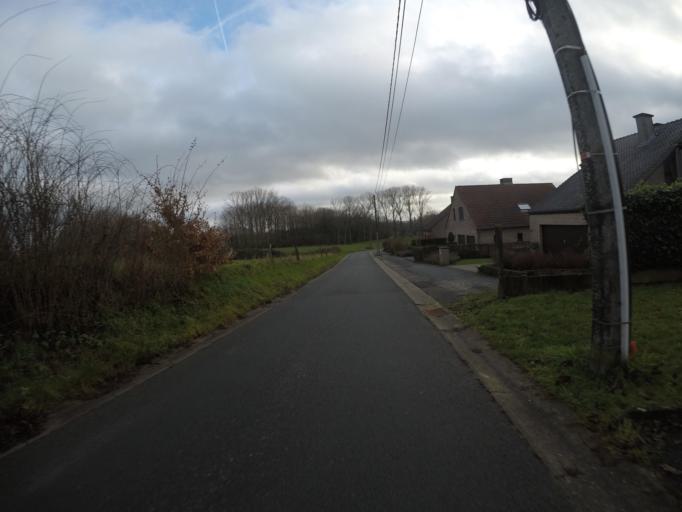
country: BE
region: Flanders
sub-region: Provincie Vlaams-Brabant
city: Gooik
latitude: 50.7942
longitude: 4.1306
